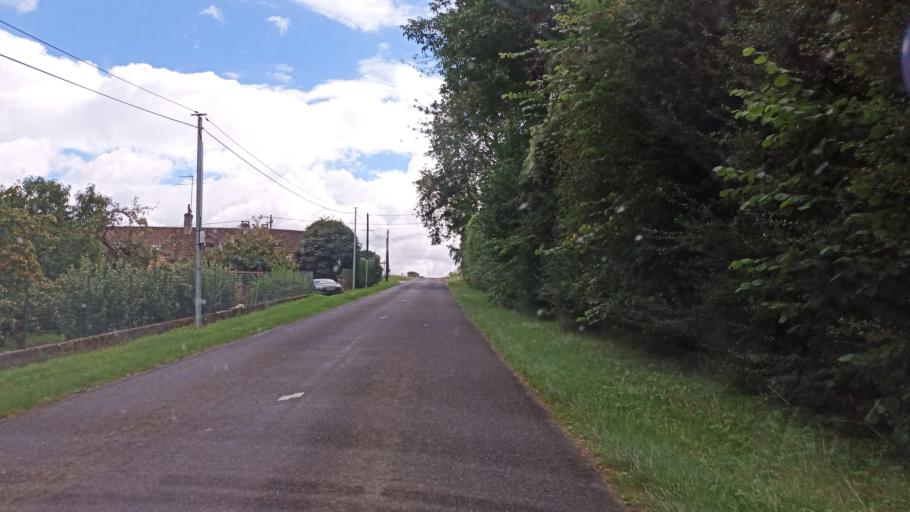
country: FR
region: Bourgogne
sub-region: Departement de l'Yonne
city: Cheroy
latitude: 48.2523
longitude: 3.0281
